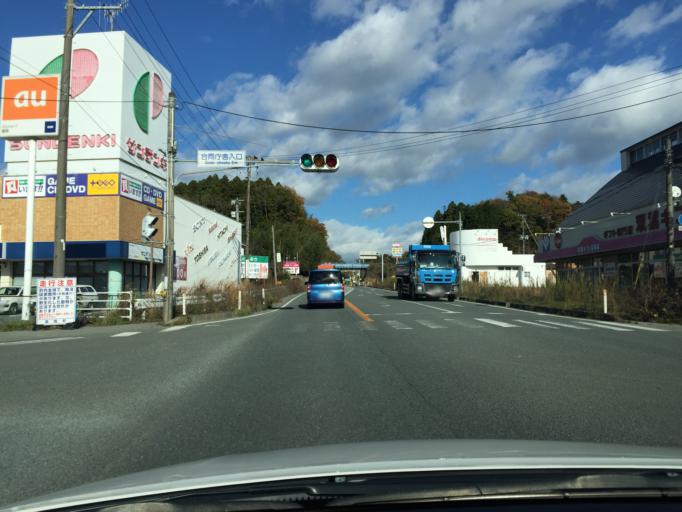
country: JP
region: Fukushima
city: Namie
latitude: 37.3431
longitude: 141.0127
